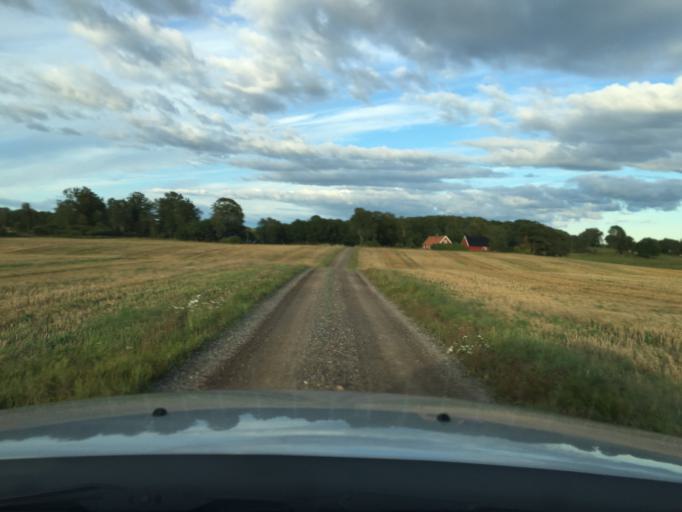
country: SE
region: Skane
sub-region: Hassleholms Kommun
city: Sosdala
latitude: 56.0287
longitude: 13.7349
